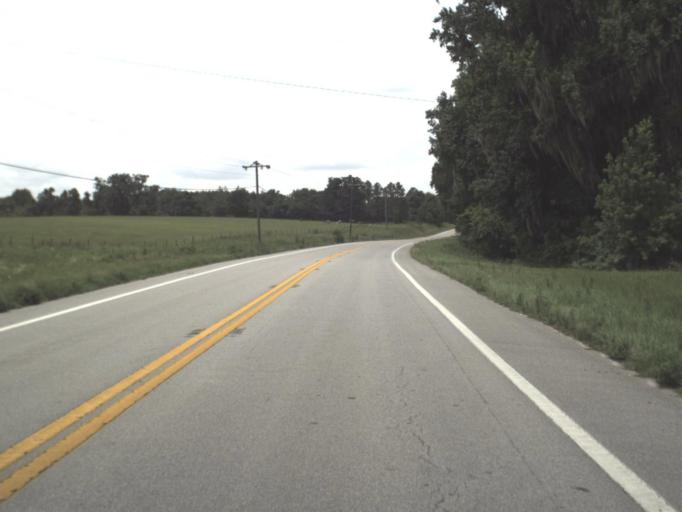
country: US
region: Florida
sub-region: Madison County
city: Madison
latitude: 30.5890
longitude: -83.4303
